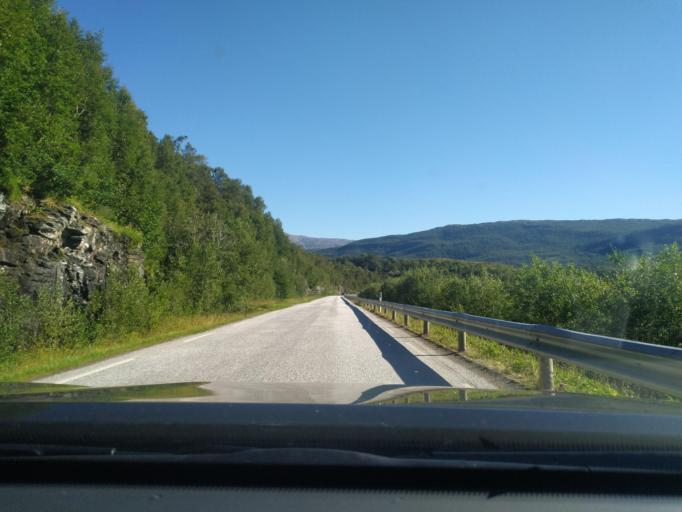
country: NO
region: Troms
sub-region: Dyroy
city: Brostadbotn
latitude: 68.9330
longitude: 17.6885
